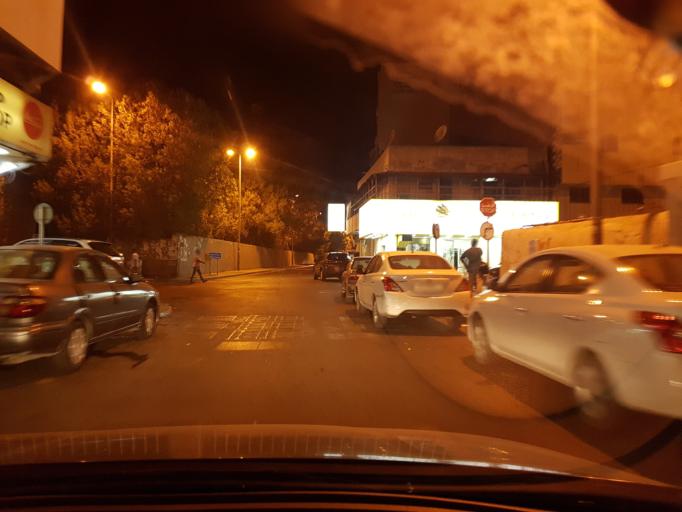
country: BH
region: Manama
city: Manama
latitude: 26.2283
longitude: 50.5855
